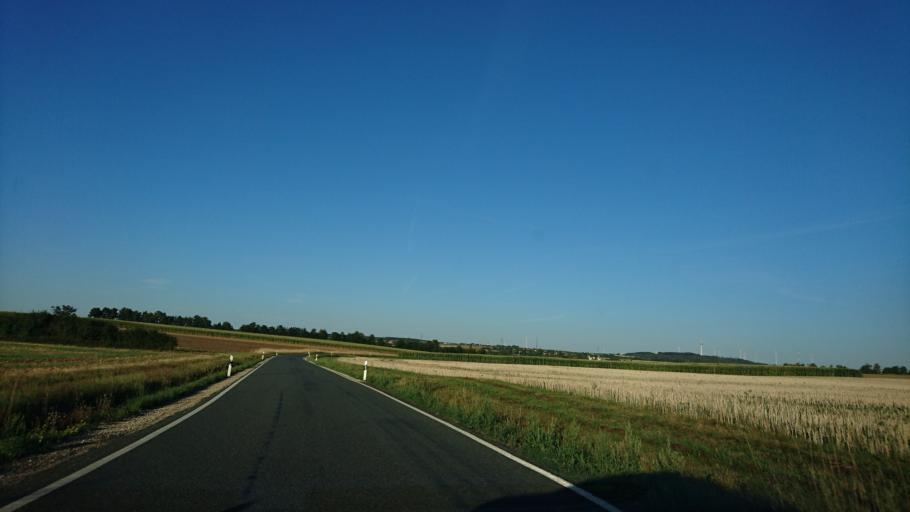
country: DE
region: Bavaria
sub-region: Regierungsbezirk Mittelfranken
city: Nennslingen
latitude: 49.0490
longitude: 11.1519
